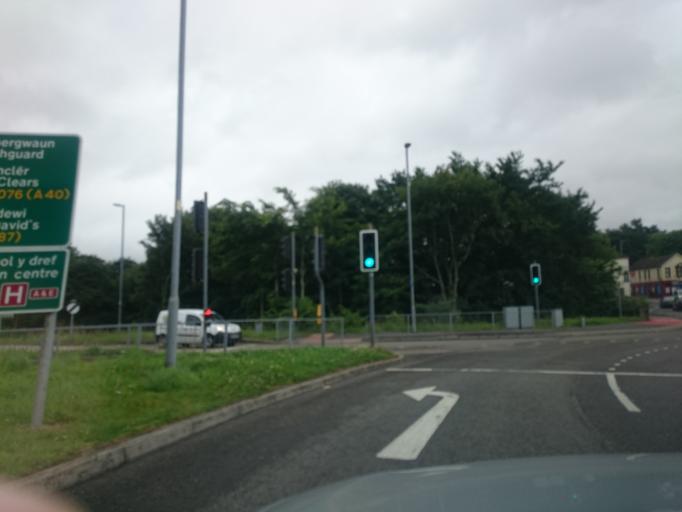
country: GB
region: Wales
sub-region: Pembrokeshire
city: Haverfordwest
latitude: 51.7923
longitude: -4.9780
